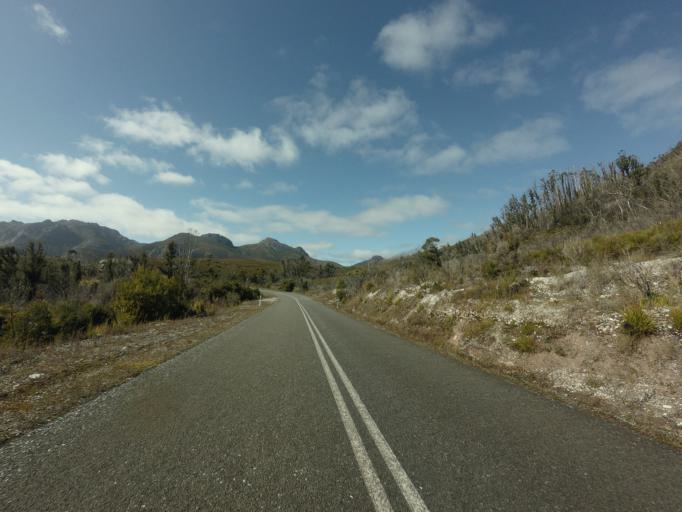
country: AU
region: Tasmania
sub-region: Huon Valley
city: Geeveston
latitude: -42.8543
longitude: 146.1883
